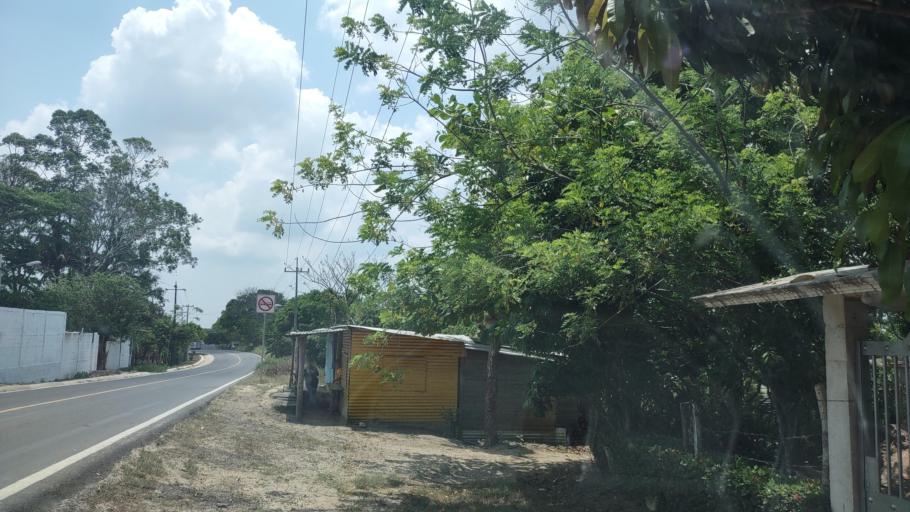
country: MX
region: Veracruz
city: Las Choapas
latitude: 17.9290
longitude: -94.1487
